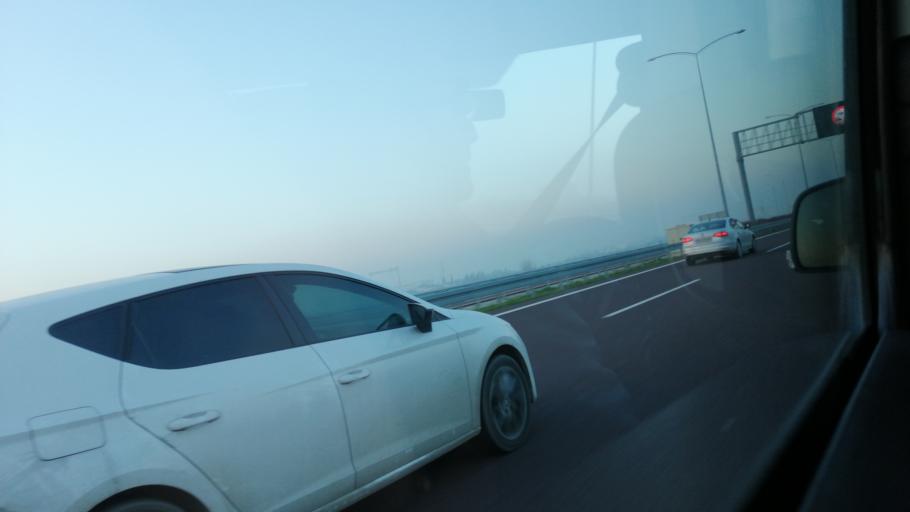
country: TR
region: Yalova
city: Altinova
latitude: 40.7109
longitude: 29.4969
